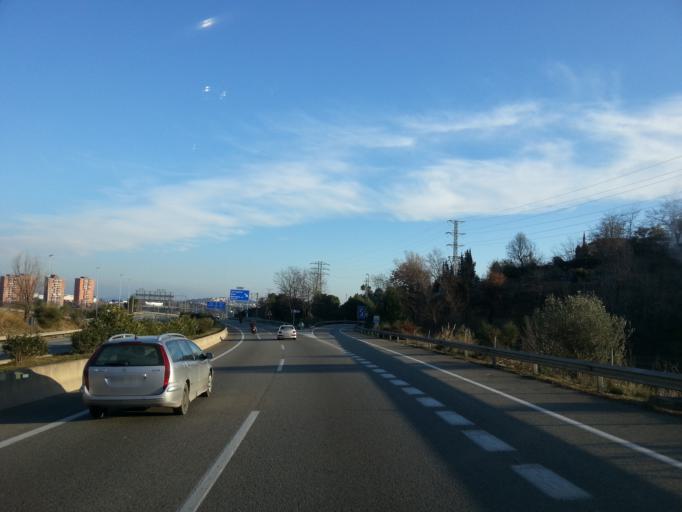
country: ES
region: Catalonia
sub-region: Provincia de Barcelona
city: Terrassa
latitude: 41.5491
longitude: 2.0070
